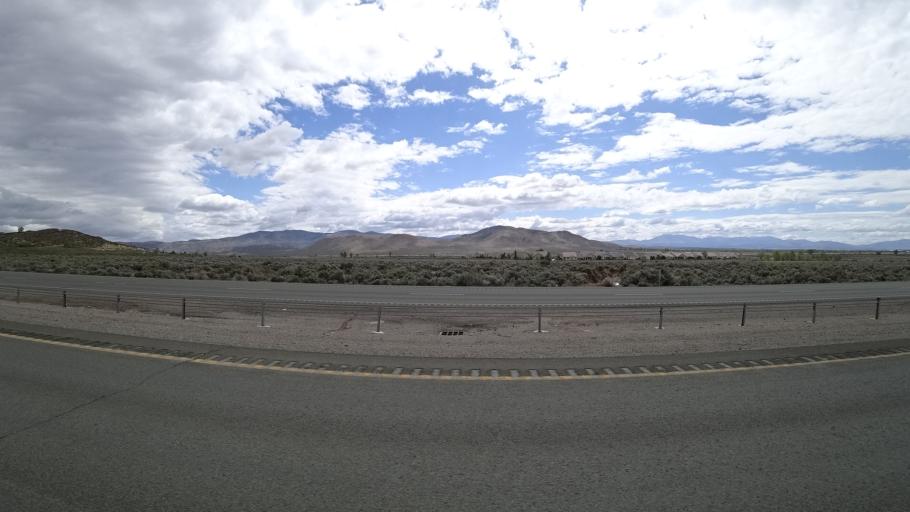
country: US
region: Nevada
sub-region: Douglas County
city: Indian Hills
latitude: 39.0788
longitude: -119.7781
